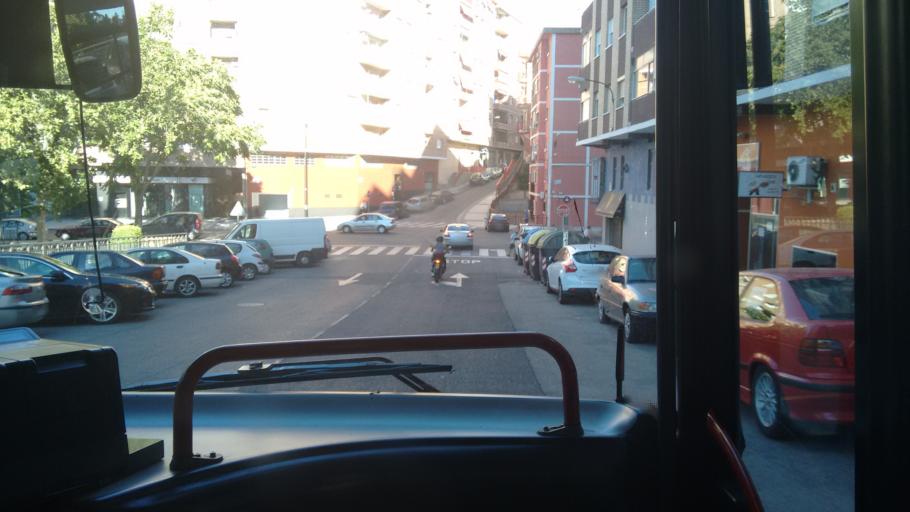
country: ES
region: Aragon
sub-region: Provincia de Zaragoza
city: Zaragoza
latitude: 41.6334
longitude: -0.8799
